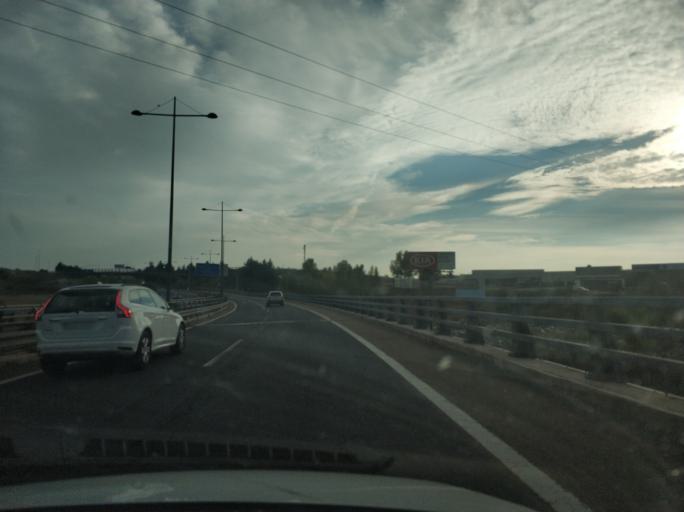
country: ES
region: Castille and Leon
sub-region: Provincia de Burgos
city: Burgos
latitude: 42.3252
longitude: -3.6993
